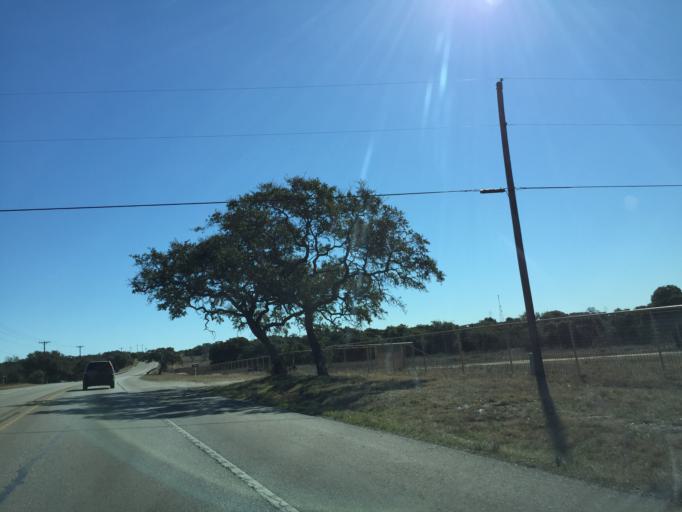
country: US
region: Texas
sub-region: Comal County
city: Canyon Lake
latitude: 29.7778
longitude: -98.3116
